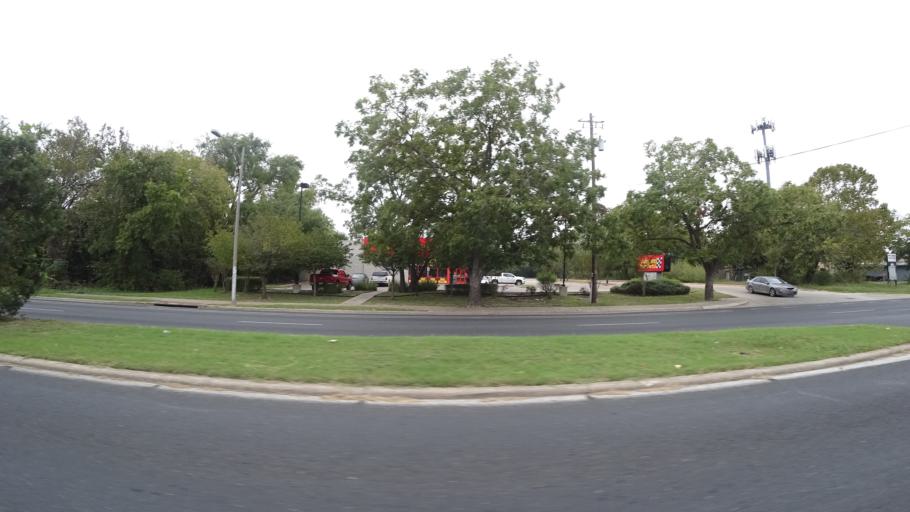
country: US
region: Texas
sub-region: Travis County
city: Austin
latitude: 30.2078
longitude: -97.7800
